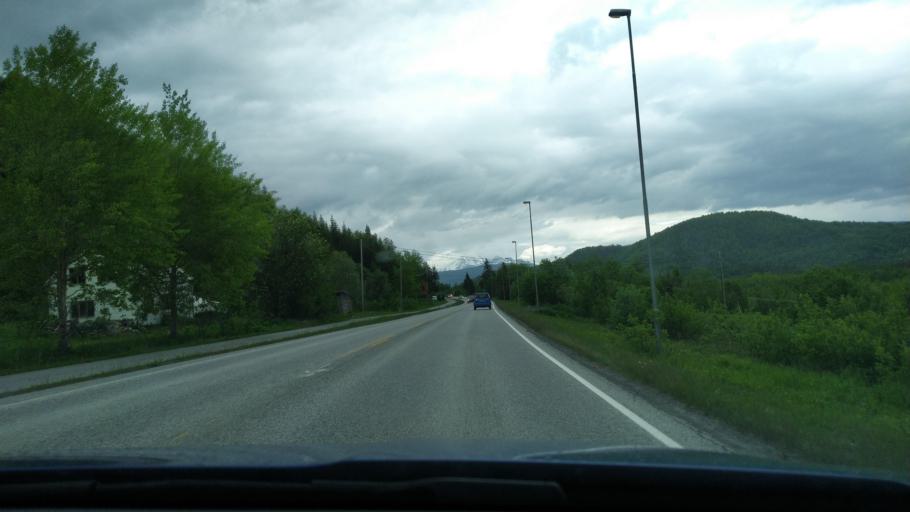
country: NO
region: Troms
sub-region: Malselv
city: Moen
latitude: 69.0232
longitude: 18.4923
